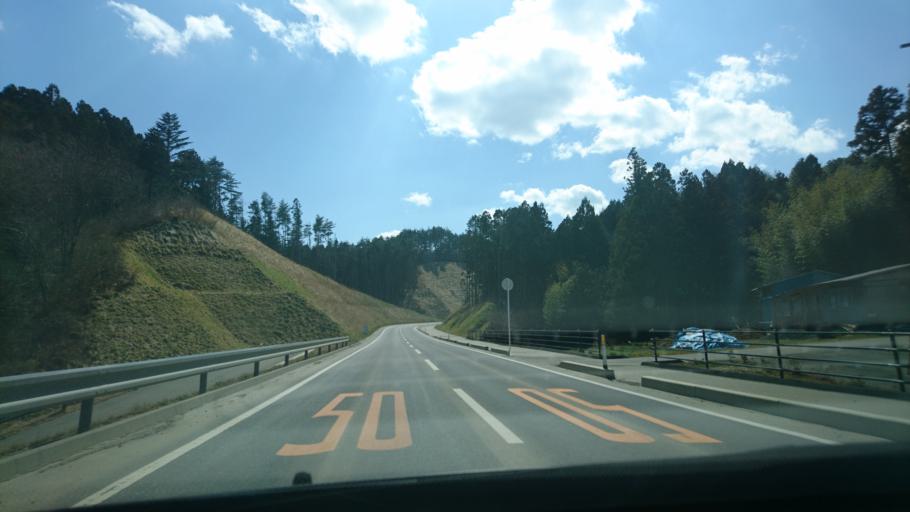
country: JP
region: Miyagi
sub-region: Oshika Gun
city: Onagawa Cho
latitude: 38.6401
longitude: 141.4497
